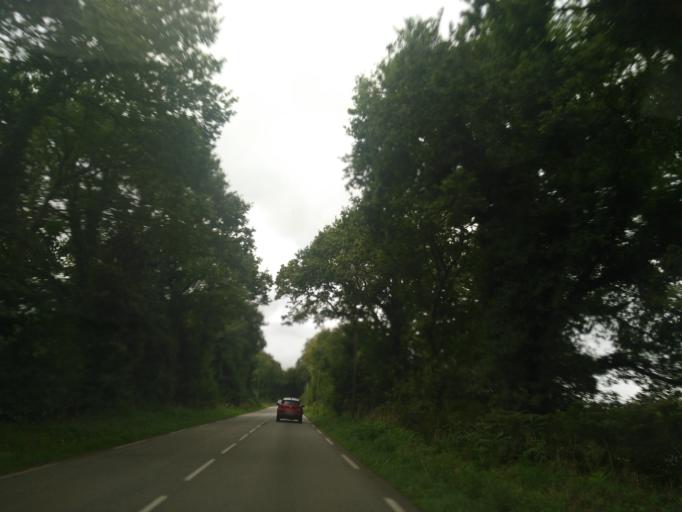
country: FR
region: Brittany
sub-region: Departement du Finistere
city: Poullan-sur-Mer
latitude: 48.0541
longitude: -4.3937
